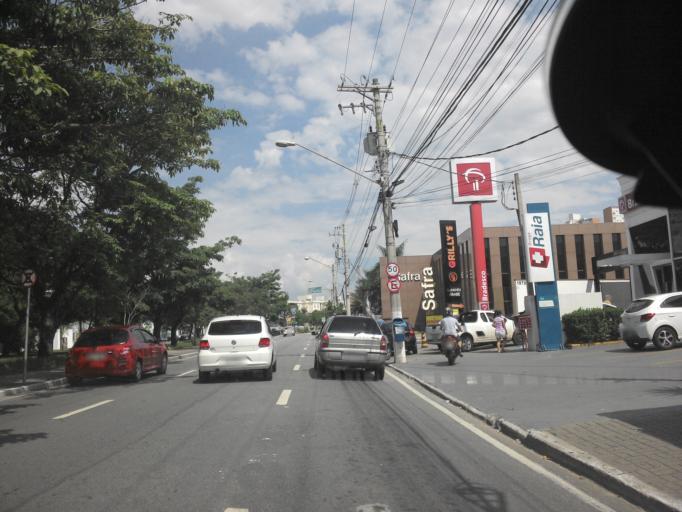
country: BR
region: Sao Paulo
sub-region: Taubate
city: Taubate
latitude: -23.0257
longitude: -45.5815
